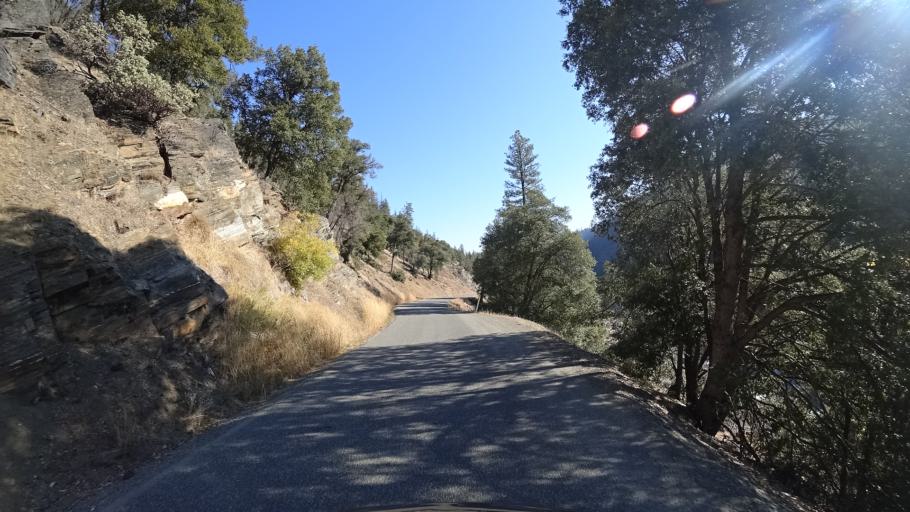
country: US
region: California
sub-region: Siskiyou County
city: Happy Camp
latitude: 41.6872
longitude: -123.0875
